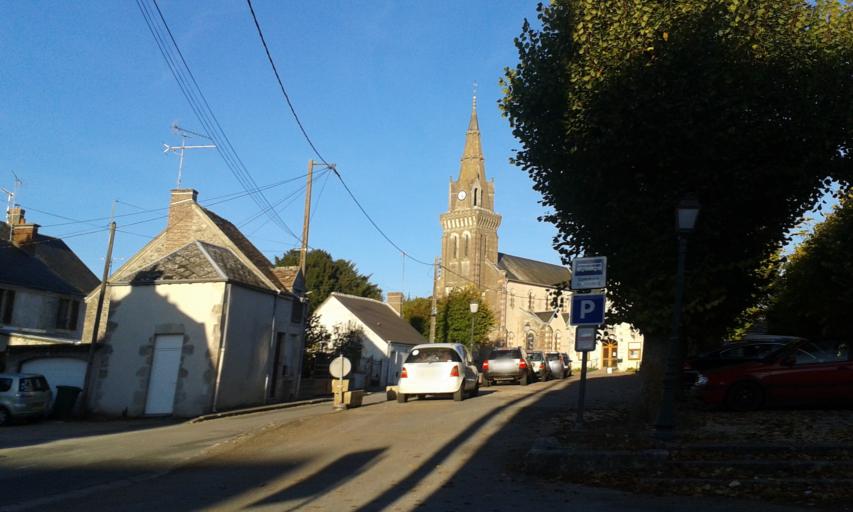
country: FR
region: Centre
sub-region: Departement du Loir-et-Cher
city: Mer
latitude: 47.7968
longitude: 1.5241
